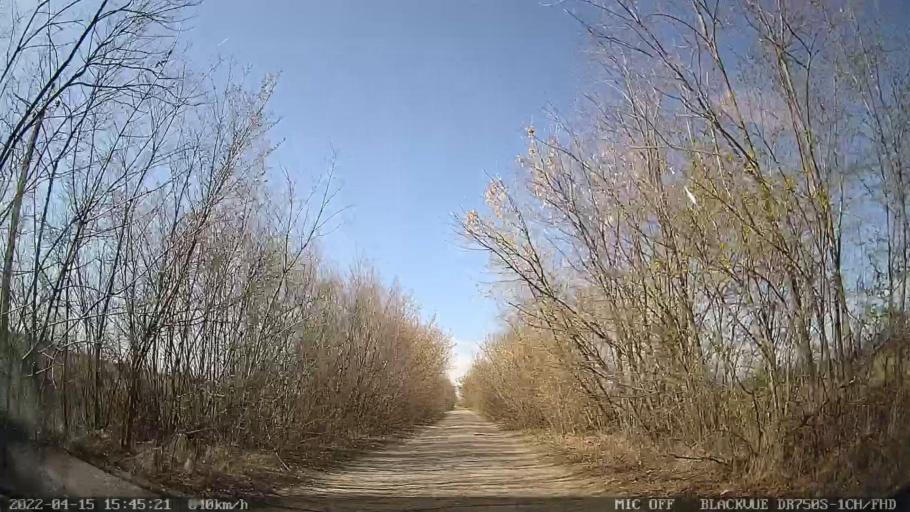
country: MD
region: Raionul Ocnita
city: Otaci
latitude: 48.3759
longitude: 27.9186
